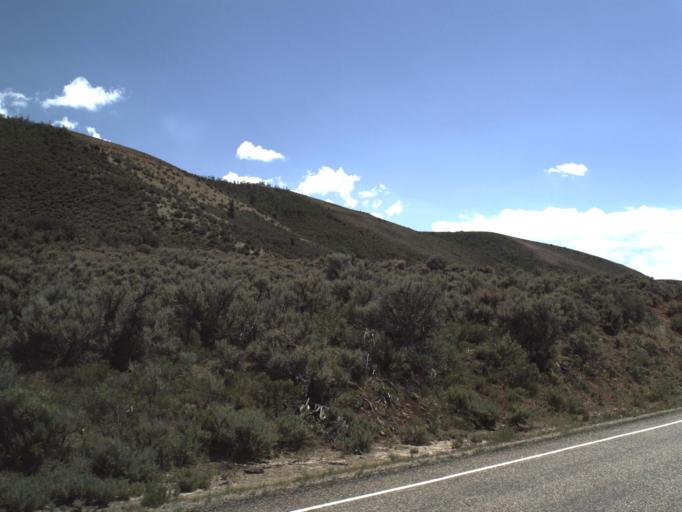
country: US
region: Utah
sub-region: Rich County
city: Randolph
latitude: 41.4955
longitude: -111.3271
